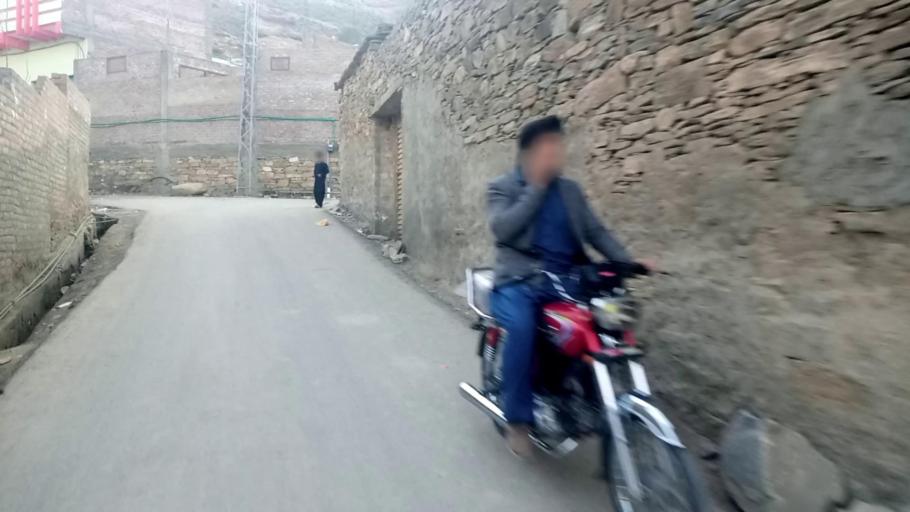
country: PK
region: Khyber Pakhtunkhwa
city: Saidu Sharif
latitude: 34.7392
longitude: 72.3516
